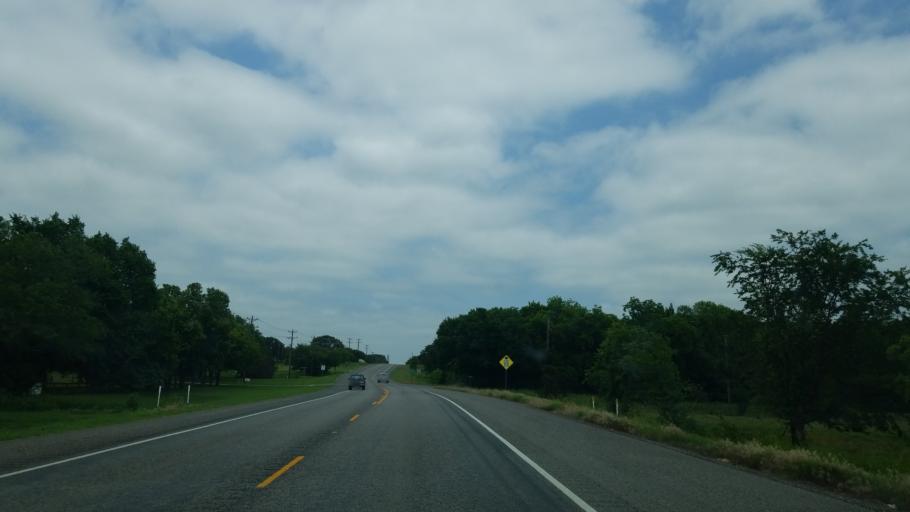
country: US
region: Texas
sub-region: Denton County
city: Aubrey
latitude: 33.3054
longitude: -97.0298
